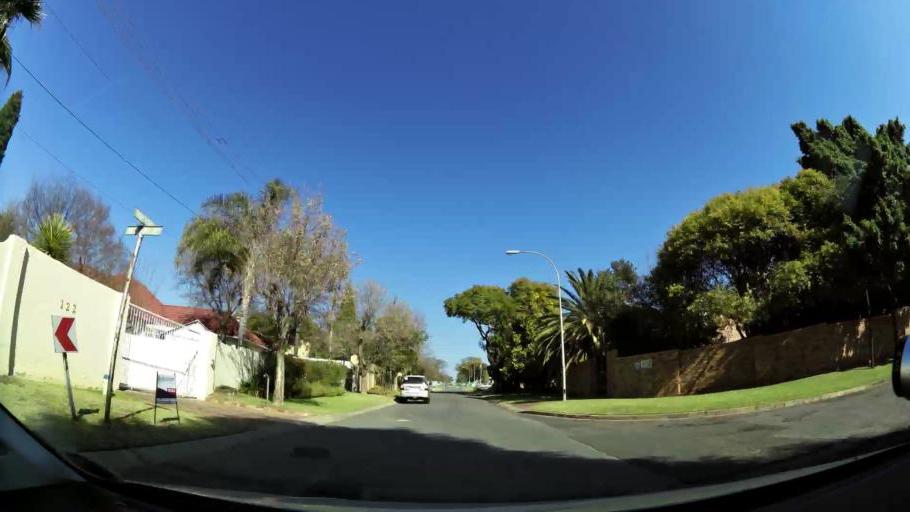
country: ZA
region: Gauteng
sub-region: City of Johannesburg Metropolitan Municipality
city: Modderfontein
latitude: -26.1354
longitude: 28.1148
